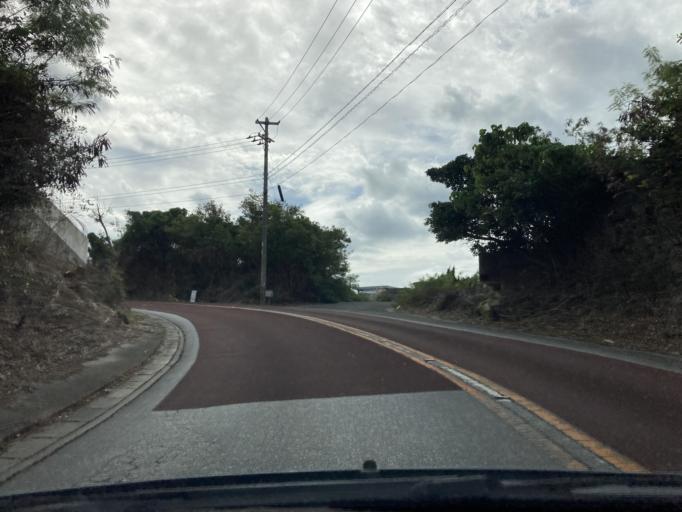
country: JP
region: Okinawa
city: Itoman
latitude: 26.1224
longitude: 127.6781
